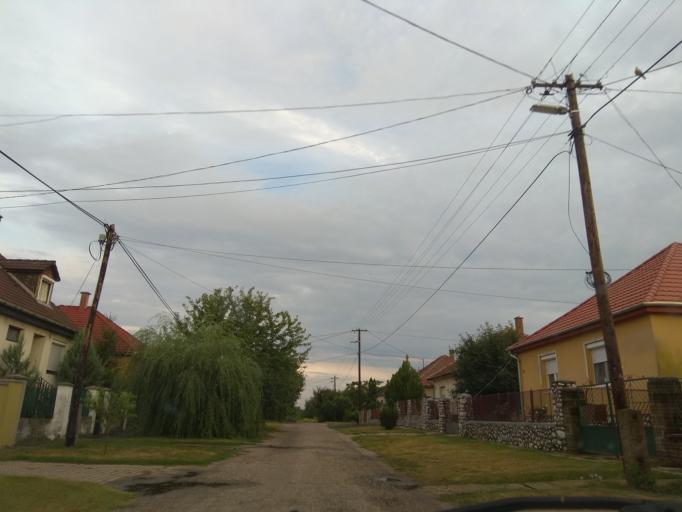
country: HU
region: Borsod-Abauj-Zemplen
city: Miskolc
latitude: 48.0749
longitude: 20.8232
